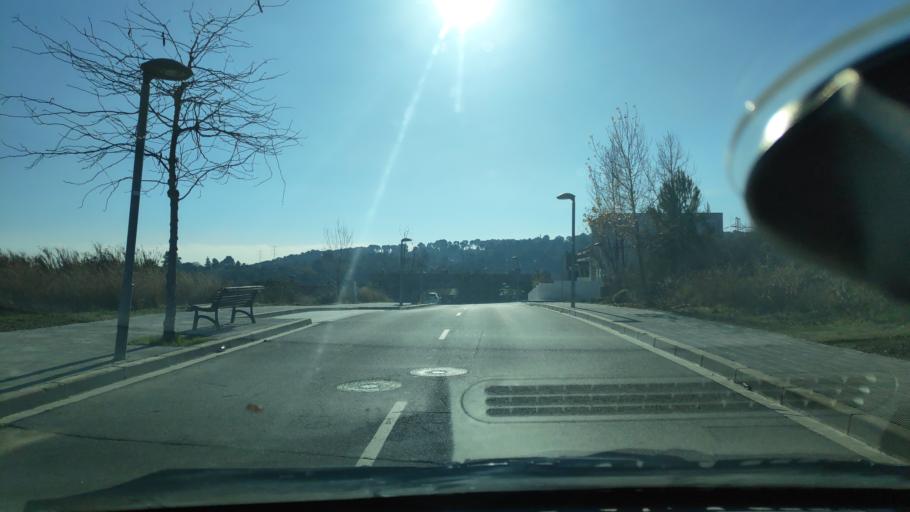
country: ES
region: Catalonia
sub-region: Provincia de Barcelona
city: Sant Quirze del Valles
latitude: 41.5249
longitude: 2.0831
